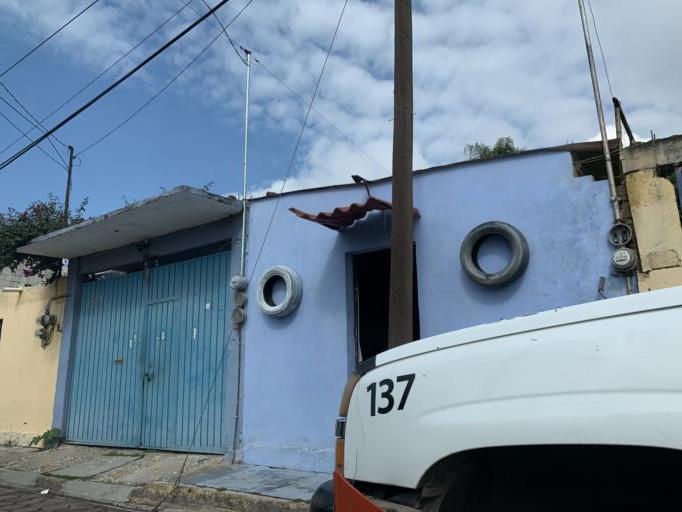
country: MX
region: Puebla
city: Cholula
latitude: 19.0717
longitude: -98.2950
